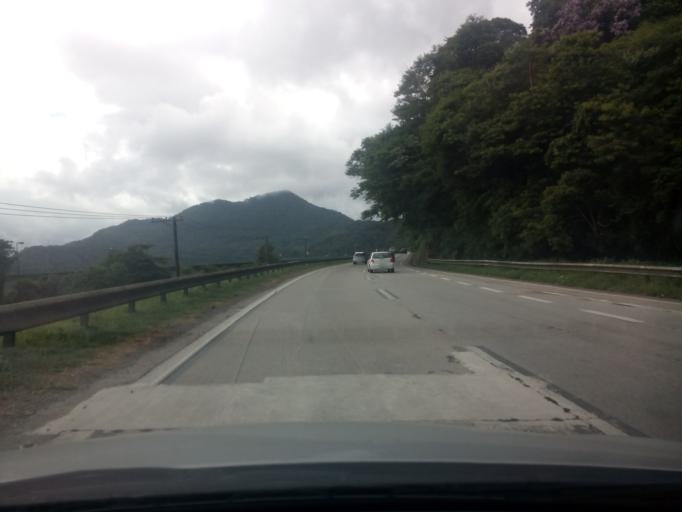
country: BR
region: Sao Paulo
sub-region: Cubatao
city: Cubatao
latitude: -23.9003
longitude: -46.4540
